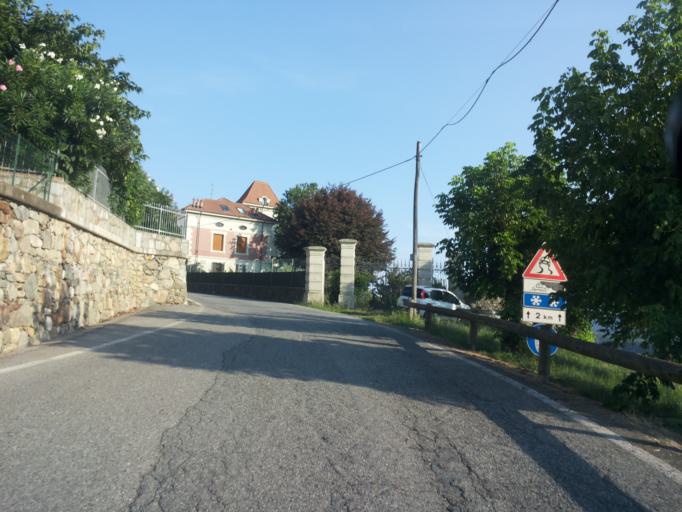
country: IT
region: Piedmont
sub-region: Provincia di Torino
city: Piverone
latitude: 45.4454
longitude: 8.0096
